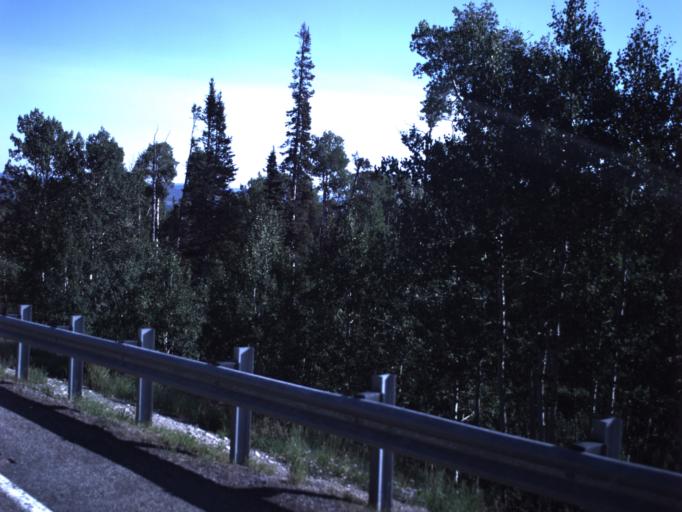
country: US
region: Utah
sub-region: Sanpete County
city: Fairview
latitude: 39.6329
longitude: -111.3254
